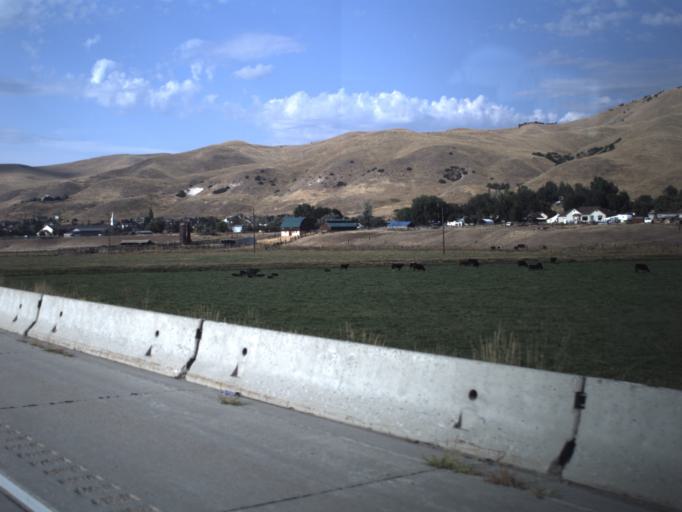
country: US
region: Utah
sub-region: Morgan County
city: Mountain Green
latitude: 41.0971
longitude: -111.7408
